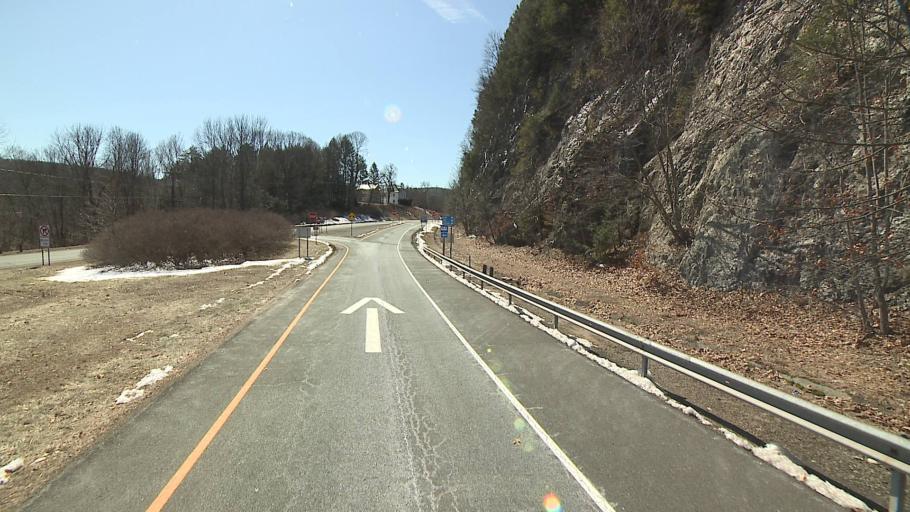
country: US
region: Connecticut
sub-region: Litchfield County
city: Thomaston
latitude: 41.6825
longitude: -73.0677
